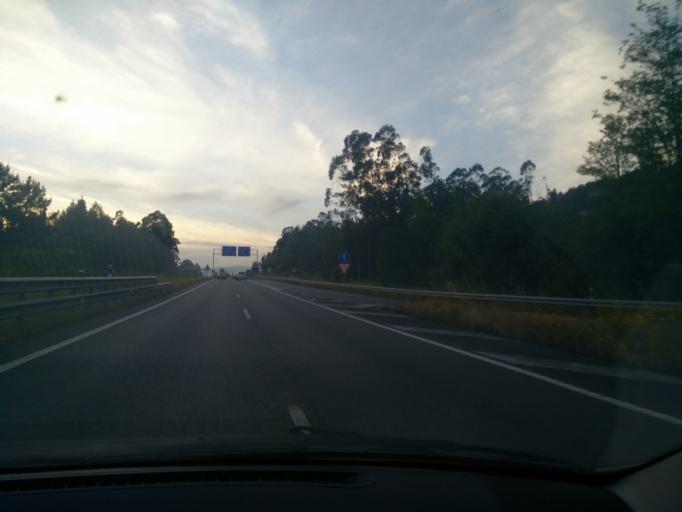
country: ES
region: Galicia
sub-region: Provincia de Pontevedra
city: Porrino
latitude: 42.1630
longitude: -8.6113
